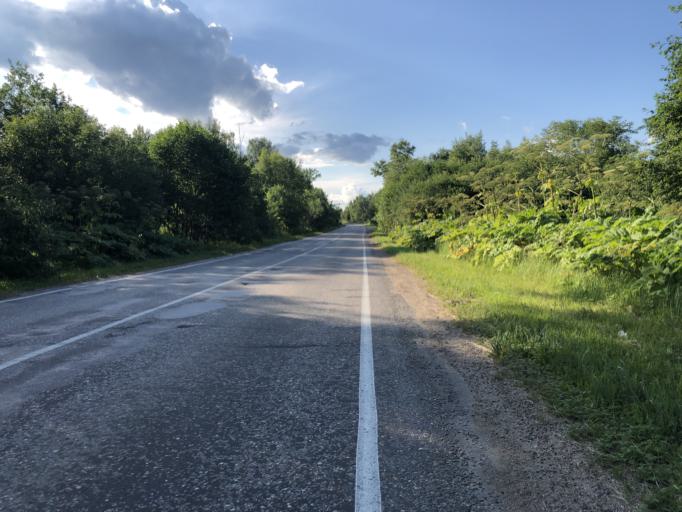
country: RU
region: Tverskaya
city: Rzhev
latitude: 56.2706
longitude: 34.2472
